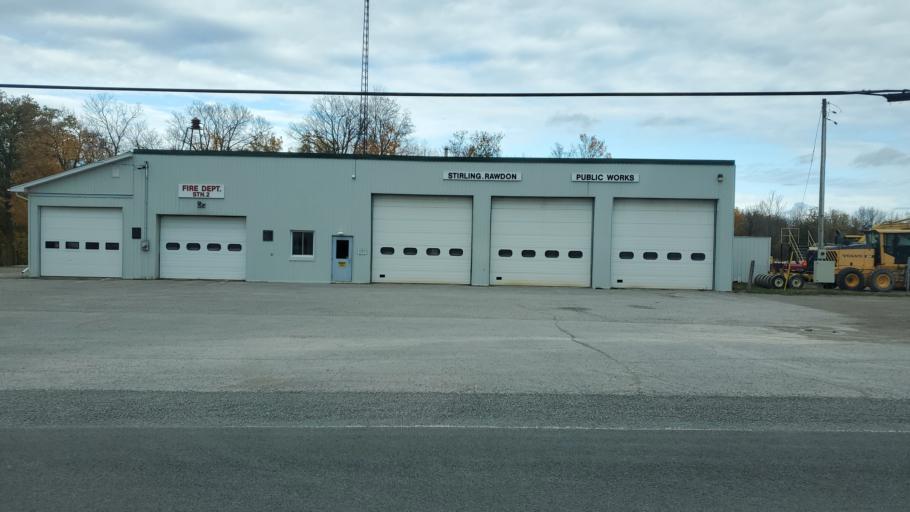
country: CA
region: Ontario
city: Quinte West
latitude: 44.4008
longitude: -77.6106
